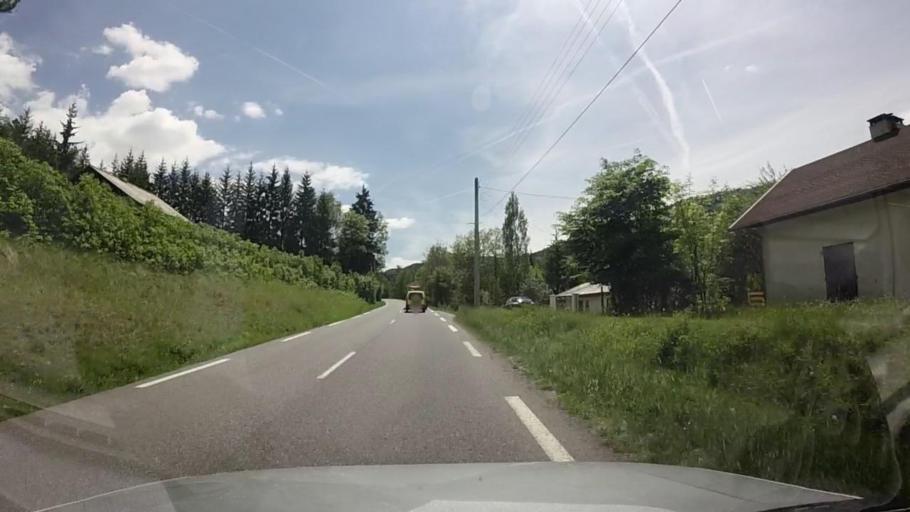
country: FR
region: Provence-Alpes-Cote d'Azur
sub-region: Departement des Alpes-de-Haute-Provence
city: Seyne-les-Alpes
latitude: 44.3297
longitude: 6.3912
